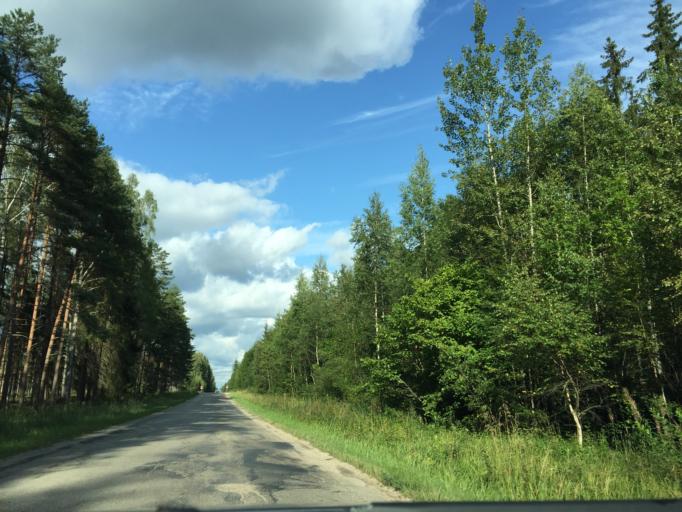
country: LV
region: Ogre
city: Ogre
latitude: 56.8330
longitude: 24.6523
